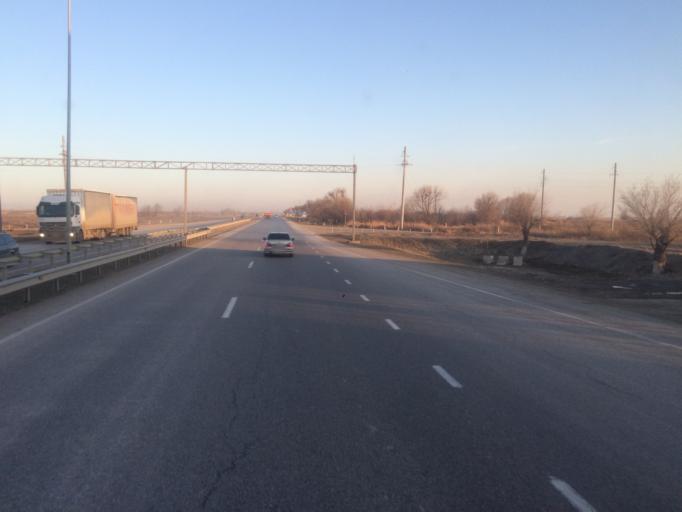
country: KZ
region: Ongtustik Qazaqstan
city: Turkestan
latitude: 43.2721
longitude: 68.3443
